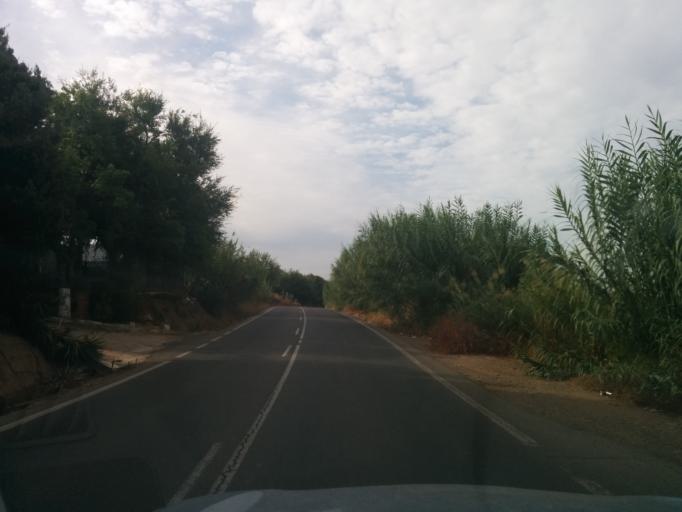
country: ES
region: Andalusia
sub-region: Provincia de Sevilla
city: La Algaba
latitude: 37.5041
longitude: -6.0242
